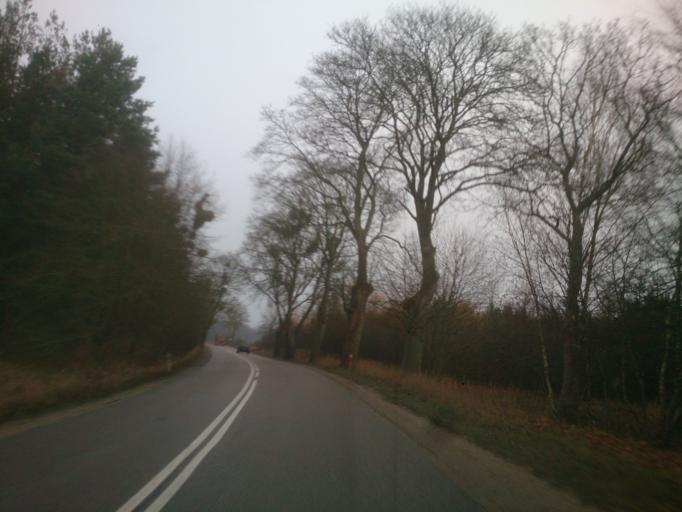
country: PL
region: Pomeranian Voivodeship
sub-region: Powiat starogardzki
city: Zblewo
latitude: 53.9185
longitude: 18.3380
